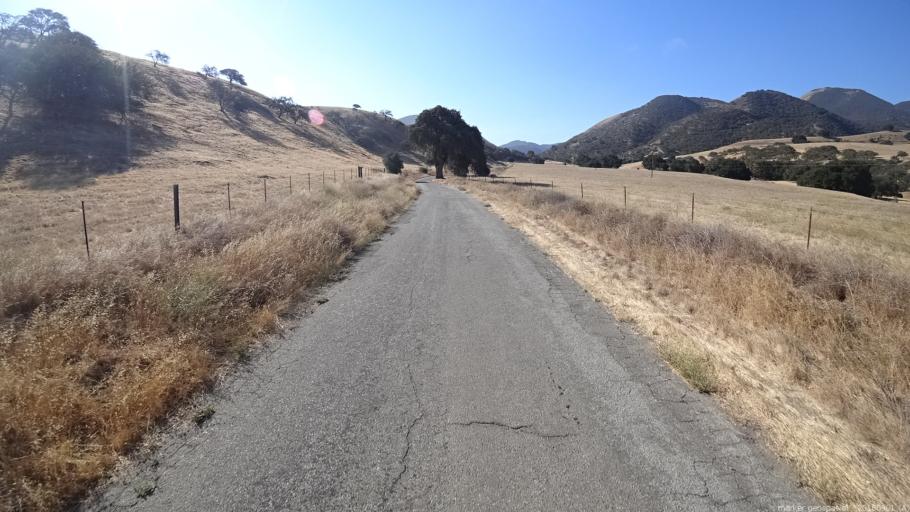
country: US
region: California
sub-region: Monterey County
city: Greenfield
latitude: 36.2472
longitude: -121.2886
